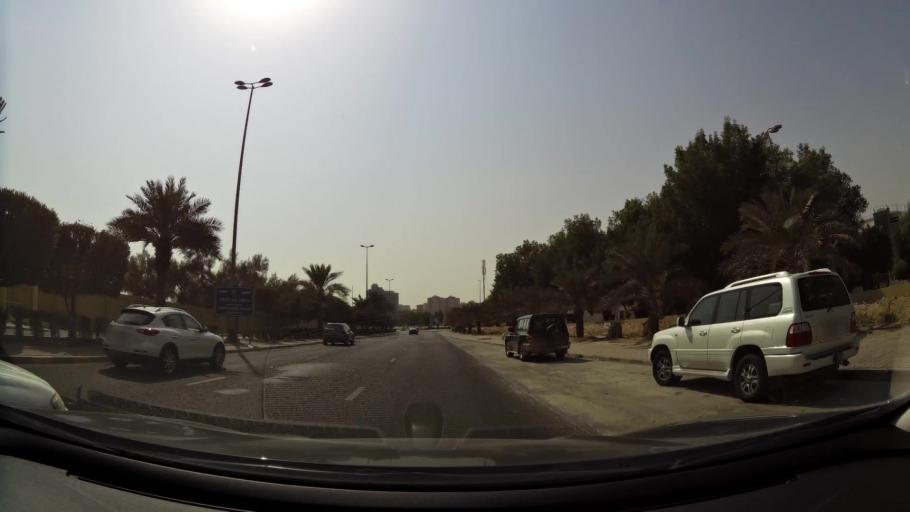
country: KW
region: Al Ahmadi
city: Al Fintas
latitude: 29.1635
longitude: 48.1225
